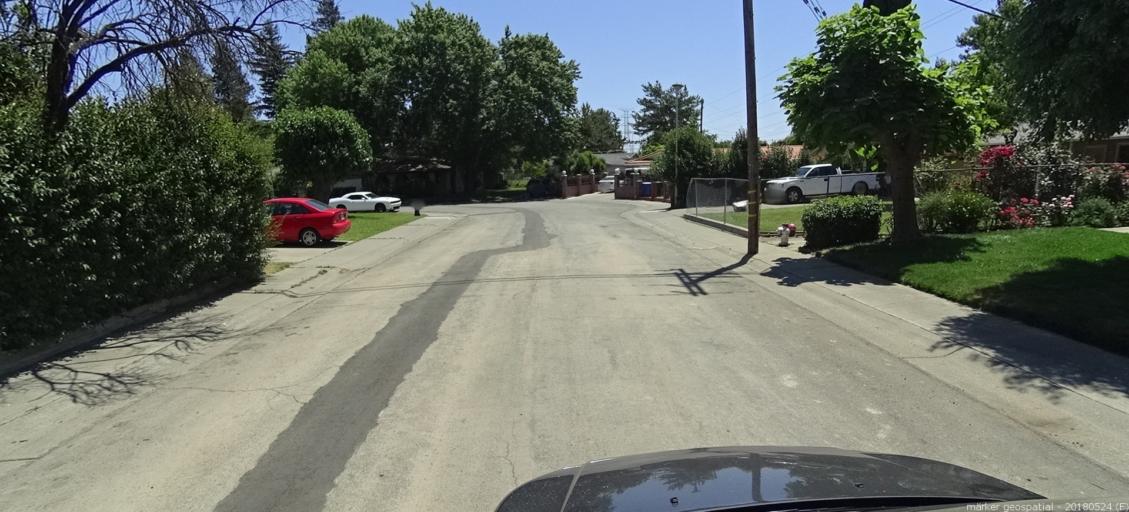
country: US
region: California
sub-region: Sacramento County
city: Sacramento
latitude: 38.6115
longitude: -121.4819
